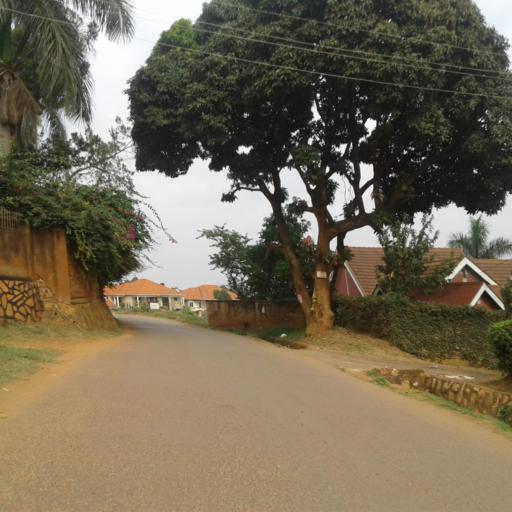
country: UG
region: Central Region
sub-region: Kampala District
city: Kampala
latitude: 0.2781
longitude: 32.6211
